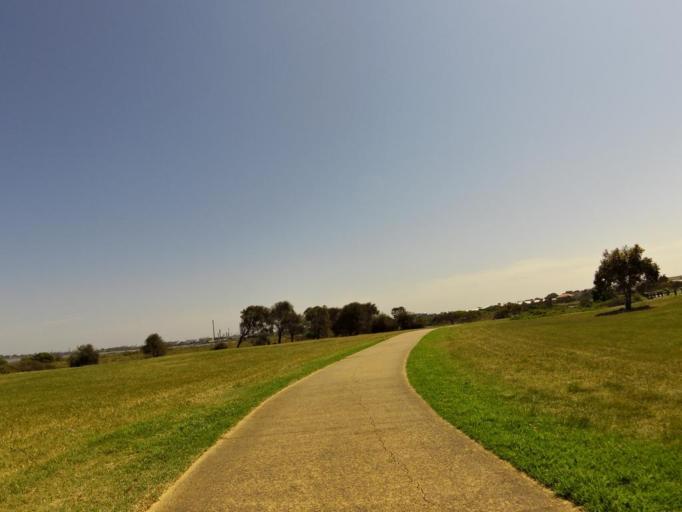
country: AU
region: Victoria
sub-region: Hobsons Bay
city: Williamstown North
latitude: -37.8629
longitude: 144.8765
